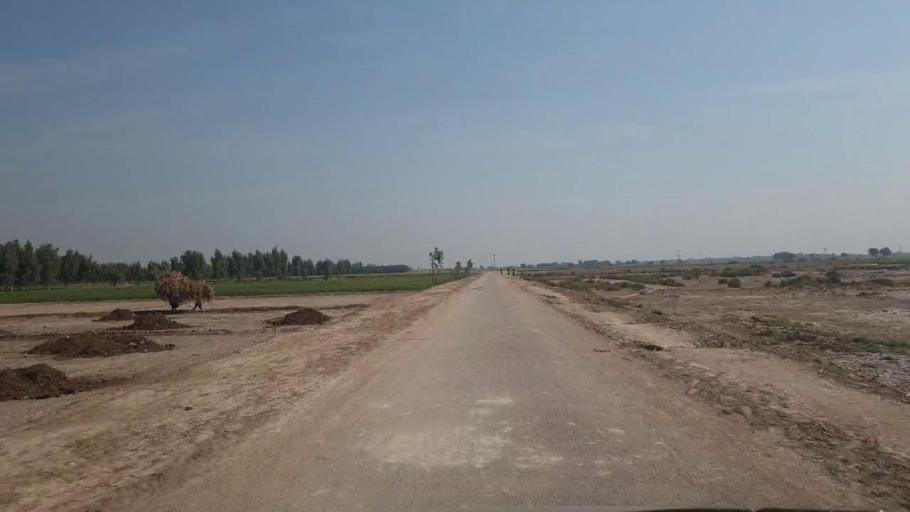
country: PK
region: Sindh
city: Chambar
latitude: 25.3736
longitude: 68.8102
